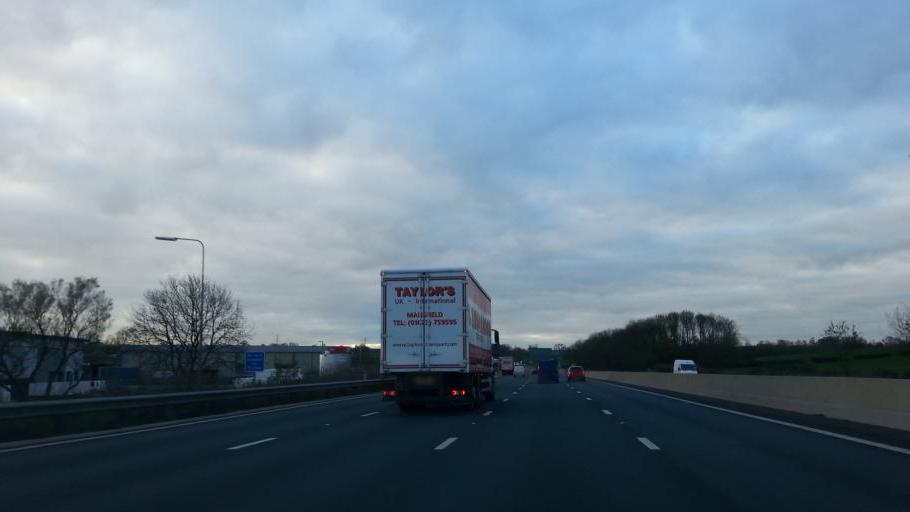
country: GB
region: England
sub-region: Northamptonshire
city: Long Buckby
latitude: 52.3495
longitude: -1.1542
